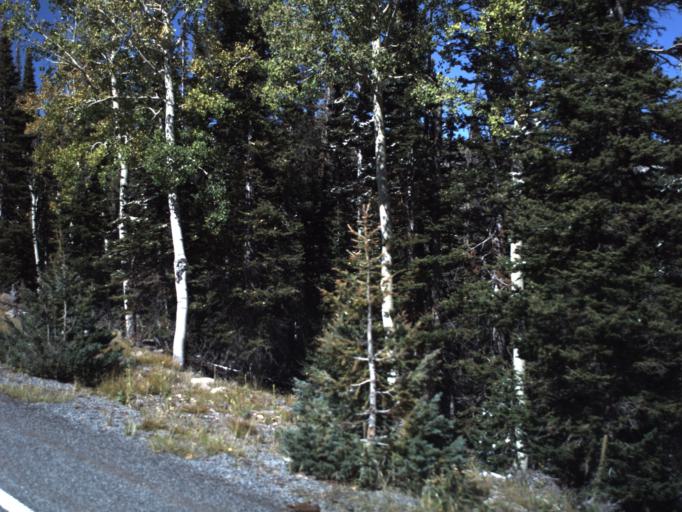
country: US
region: Utah
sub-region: Piute County
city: Junction
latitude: 38.3181
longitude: -112.3673
